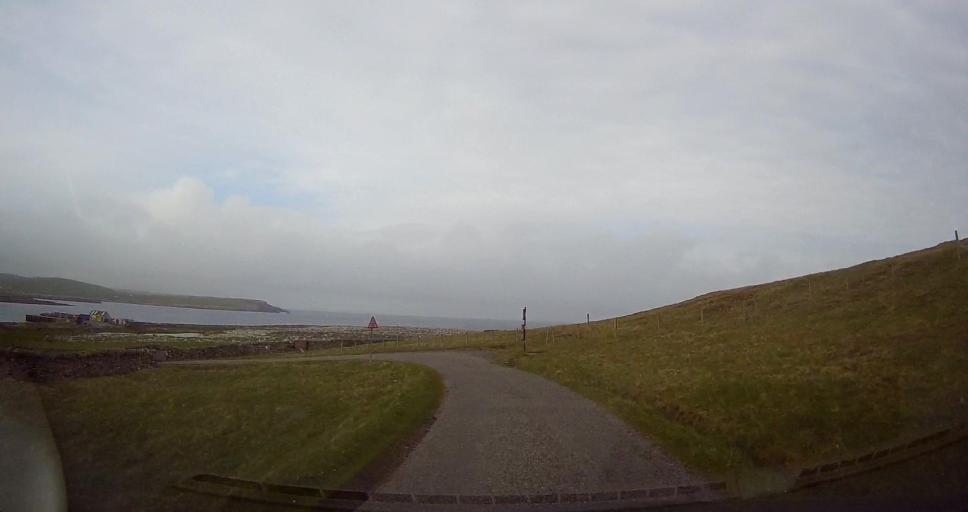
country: GB
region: Scotland
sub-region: Shetland Islands
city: Sandwick
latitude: 59.8714
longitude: -1.2778
